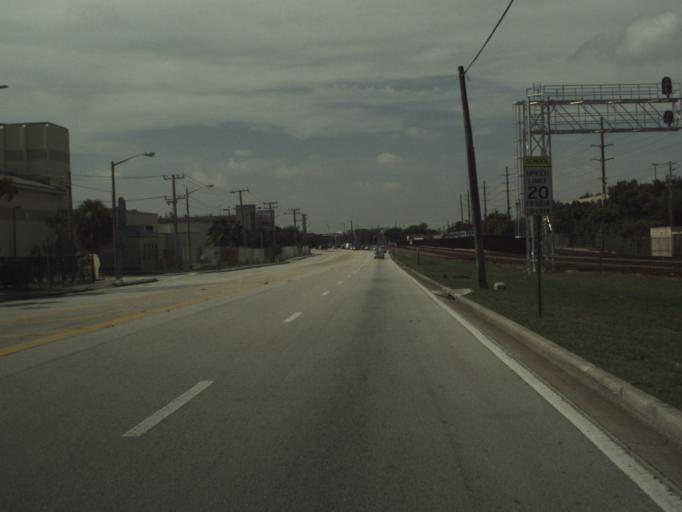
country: US
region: Florida
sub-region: Palm Beach County
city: West Palm Beach
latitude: 26.7104
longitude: -80.0621
